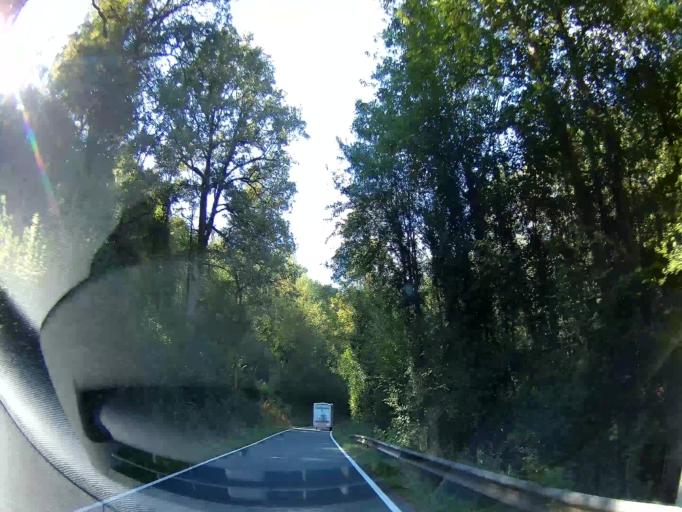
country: BE
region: Wallonia
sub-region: Province de Namur
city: Mettet
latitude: 50.3105
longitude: 4.7626
